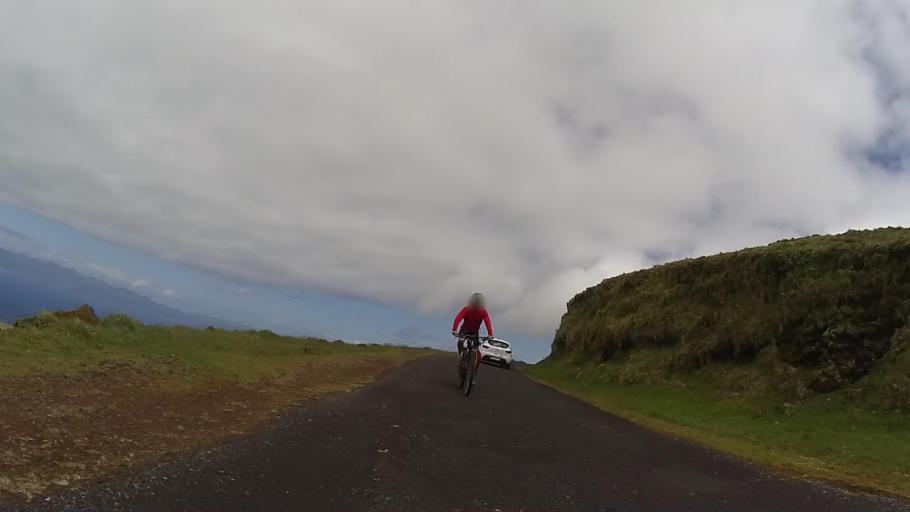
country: PT
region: Azores
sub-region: Sao Roque do Pico
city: Sao Roque do Pico
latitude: 38.4479
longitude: -28.2337
